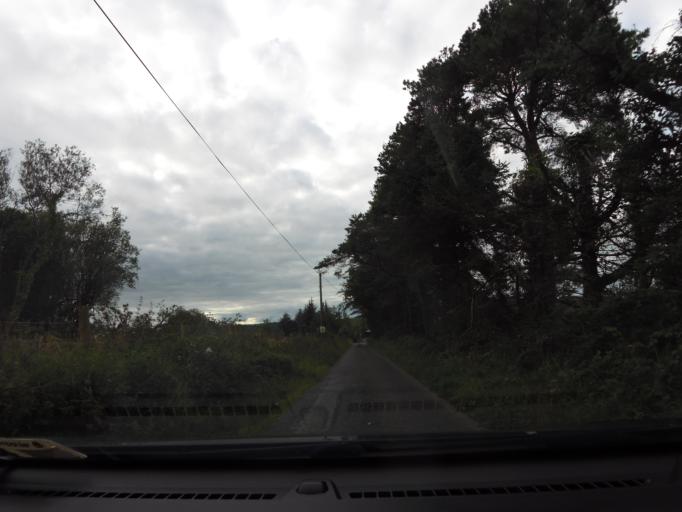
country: IE
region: Connaught
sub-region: County Galway
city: Loughrea
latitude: 53.1395
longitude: -8.5279
